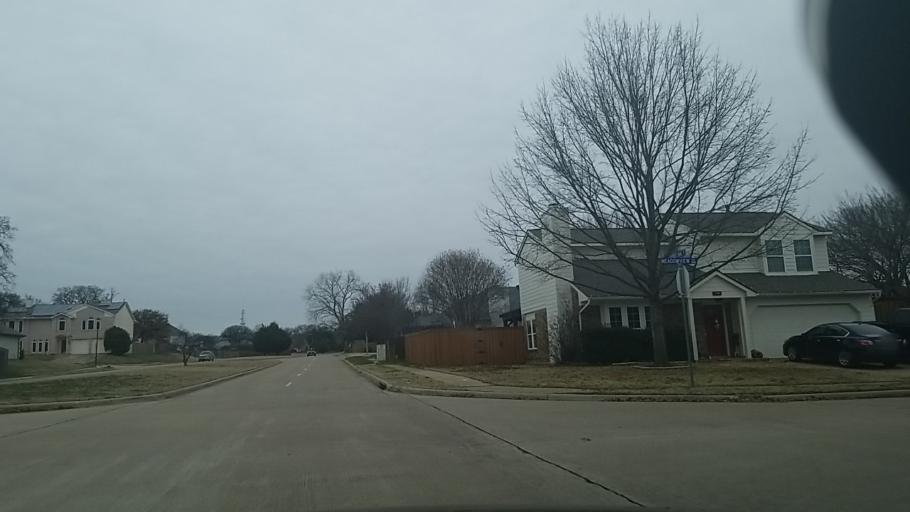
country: US
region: Texas
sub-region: Denton County
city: Corinth
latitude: 33.1381
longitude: -97.0769
